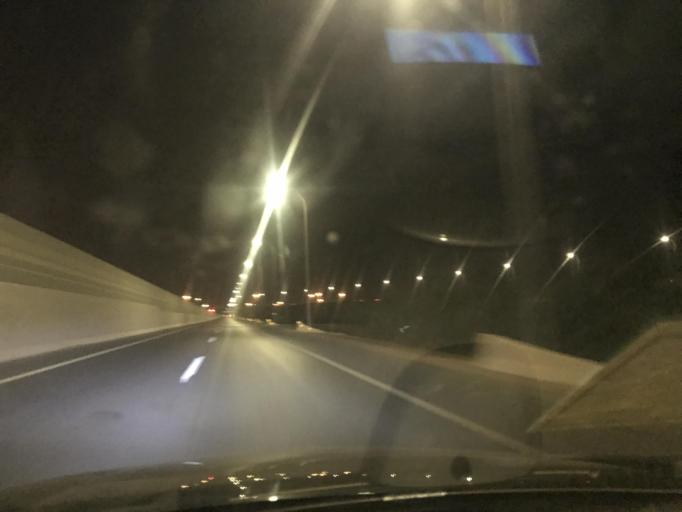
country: SA
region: Ar Riyad
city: Riyadh
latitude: 24.9081
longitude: 46.7165
